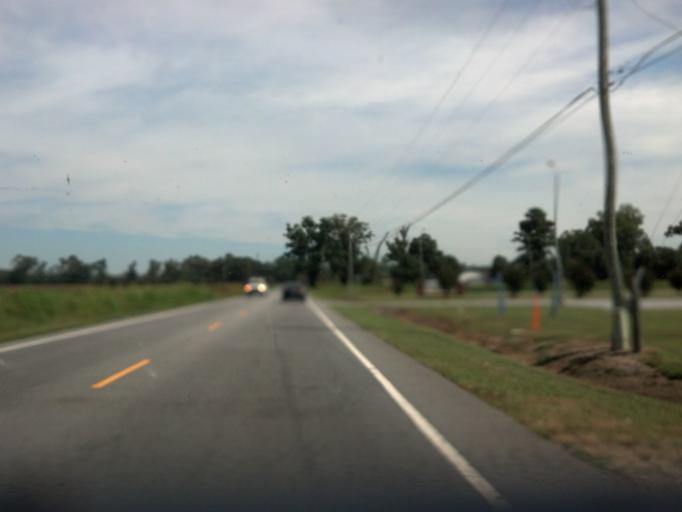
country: US
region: North Carolina
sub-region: Greene County
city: Snow Hill
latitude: 35.4724
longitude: -77.6592
